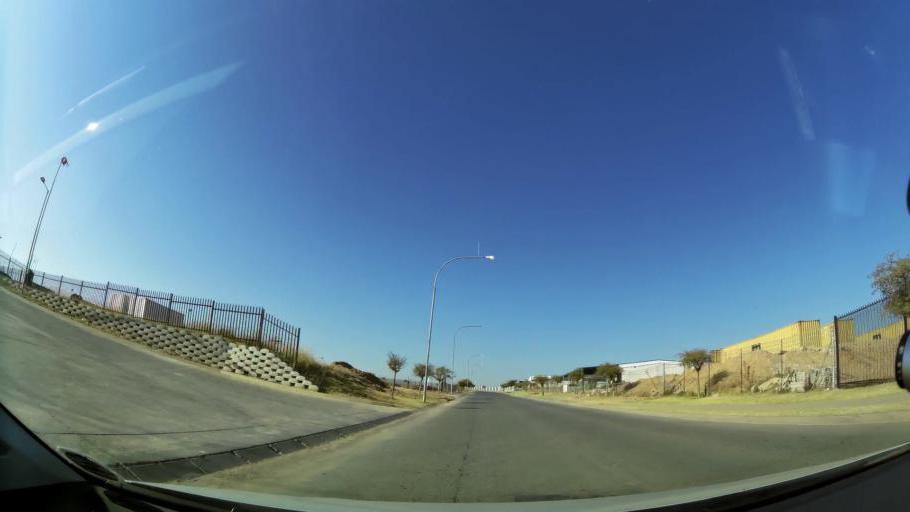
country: ZA
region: Gauteng
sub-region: City of Johannesburg Metropolitan Municipality
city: Modderfontein
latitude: -26.0531
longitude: 28.1656
